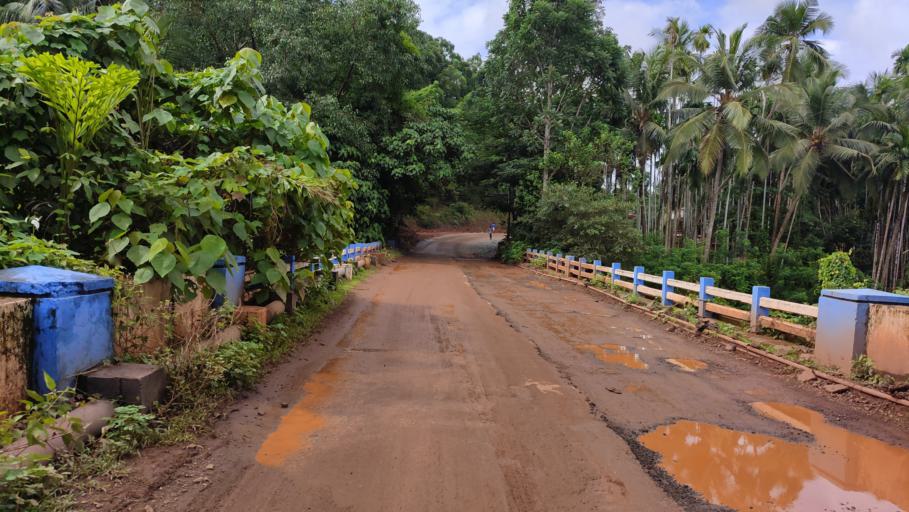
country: IN
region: Kerala
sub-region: Kasaragod District
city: Kasaragod
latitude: 12.5228
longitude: 75.0720
